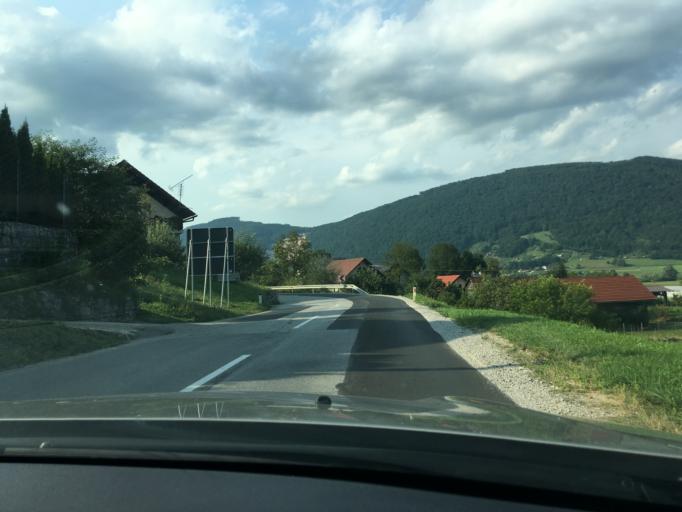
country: SI
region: Dolenjske Toplice
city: Dolenjske Toplice
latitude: 45.7601
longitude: 15.0312
